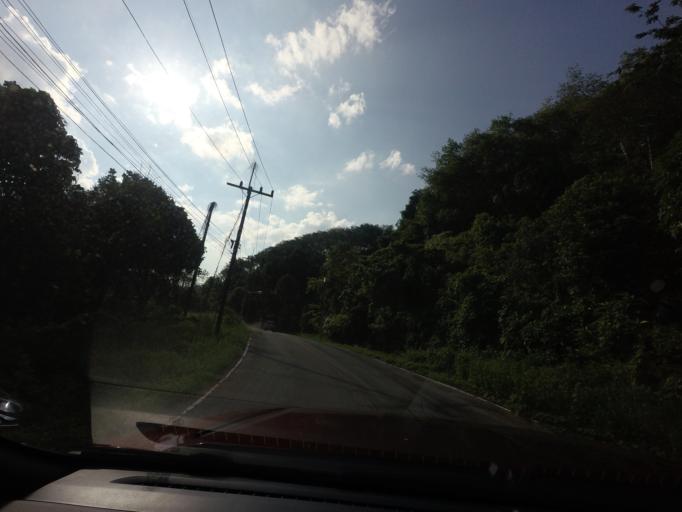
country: TH
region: Yala
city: Than To
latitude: 6.1252
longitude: 101.3027
